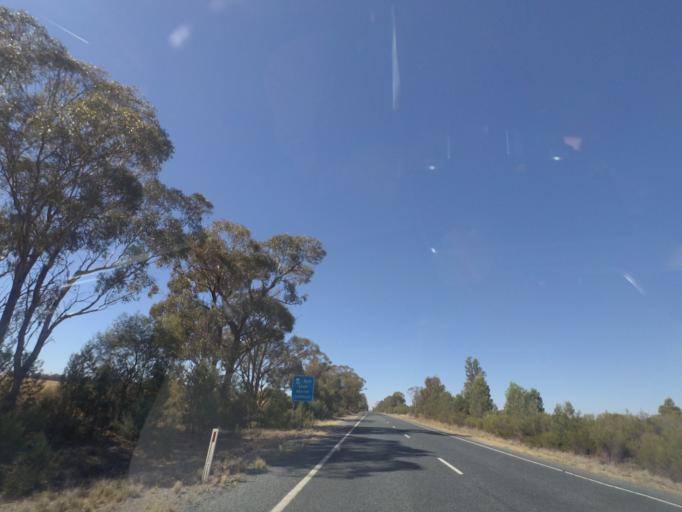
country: AU
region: New South Wales
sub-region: Bland
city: West Wyalong
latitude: -34.1565
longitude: 147.1175
